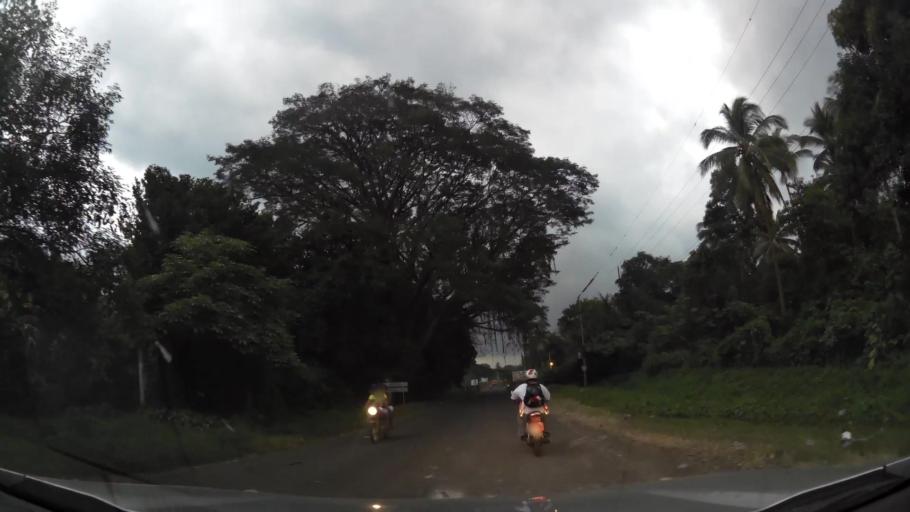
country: GT
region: Escuintla
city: Santa Lucia Cotzumalguapa
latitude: 14.3218
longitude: -91.0365
